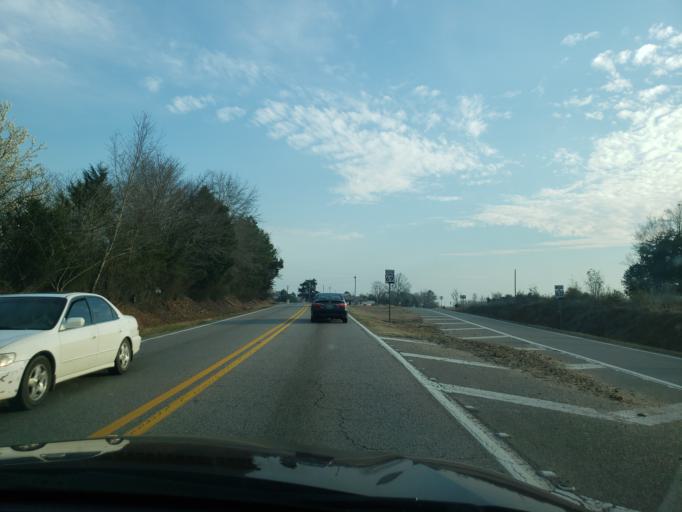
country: US
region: Alabama
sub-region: Hale County
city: Moundville
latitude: 32.9152
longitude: -87.6398
